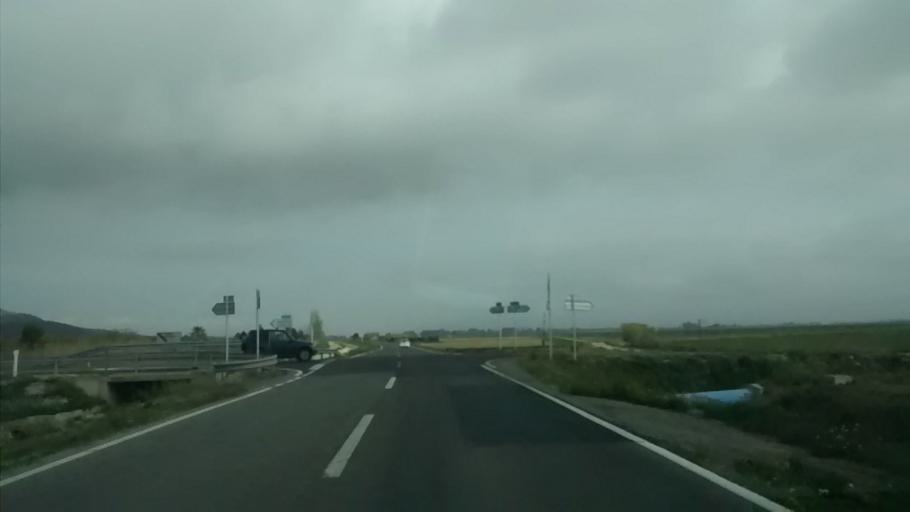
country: ES
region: Catalonia
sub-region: Provincia de Tarragona
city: Sant Carles de la Rapita
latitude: 40.6412
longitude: 0.6008
